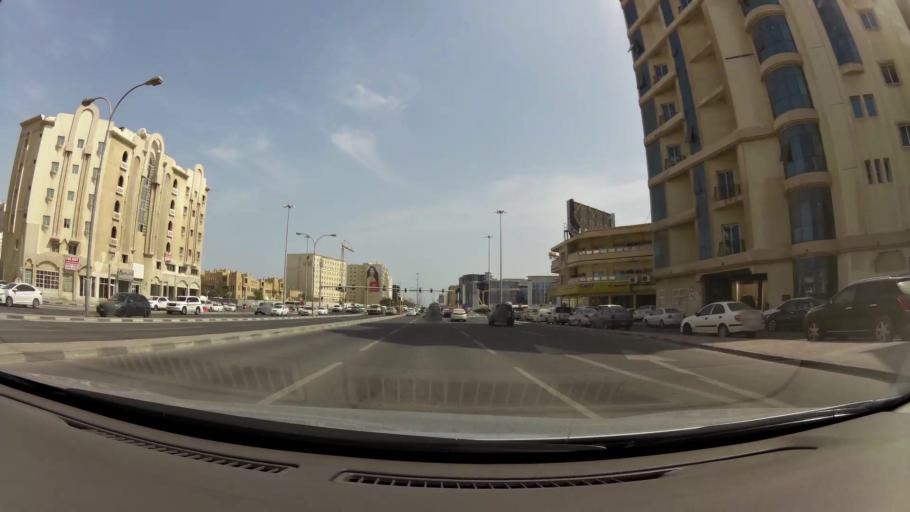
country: QA
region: Baladiyat ad Dawhah
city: Doha
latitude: 25.2768
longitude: 51.5382
